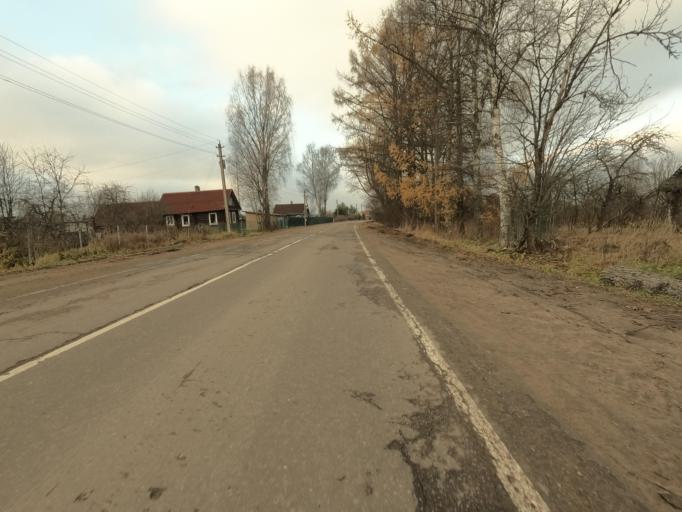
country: RU
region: Leningrad
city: Mga
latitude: 59.7734
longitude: 31.0239
